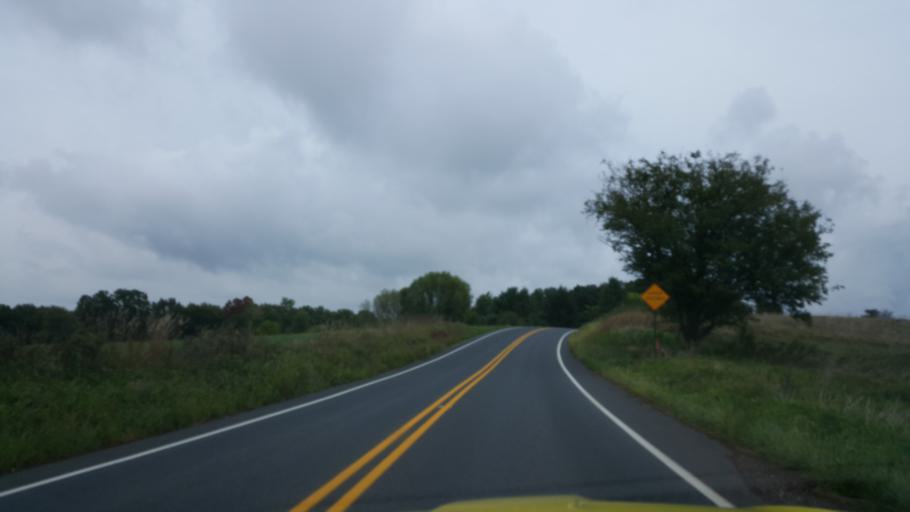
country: US
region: Pennsylvania
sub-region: Lebanon County
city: Campbelltown
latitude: 40.2341
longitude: -76.5470
